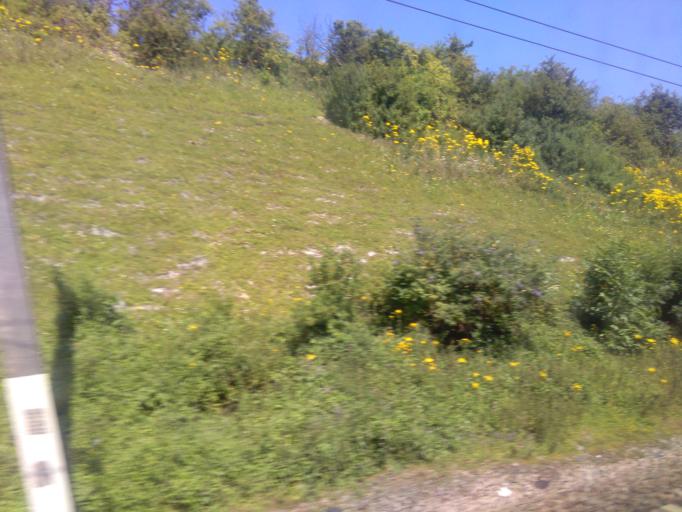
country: GB
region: England
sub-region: Luton
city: Luton
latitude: 51.8695
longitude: -0.3900
